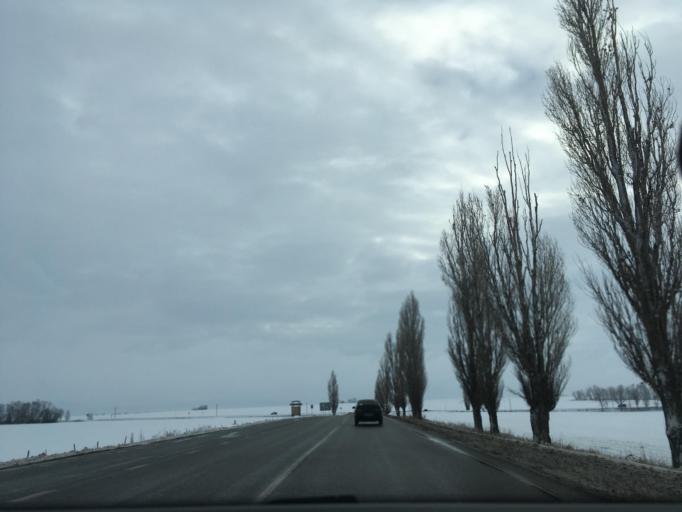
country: UA
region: Luhansk
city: Lozno-Oleksandrivka
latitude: 49.9539
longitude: 38.9523
